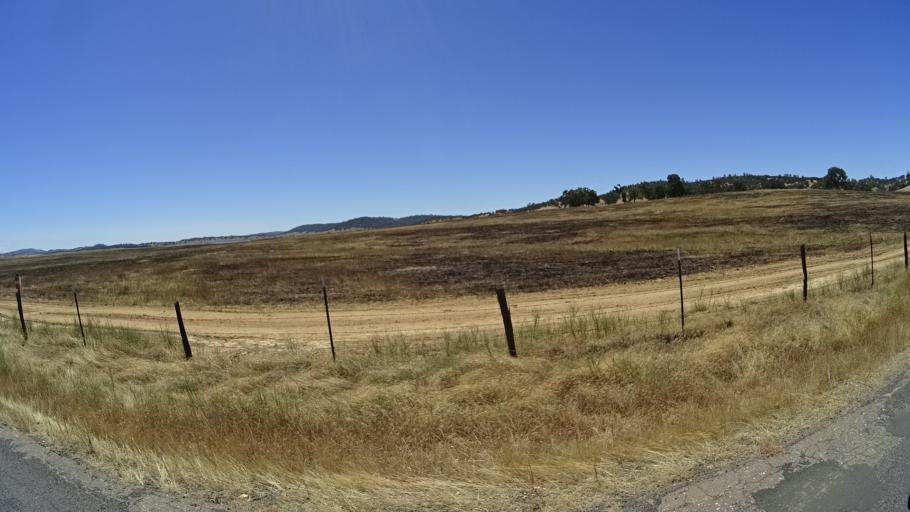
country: US
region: California
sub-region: Calaveras County
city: Rancho Calaveras
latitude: 38.0573
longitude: -120.7687
